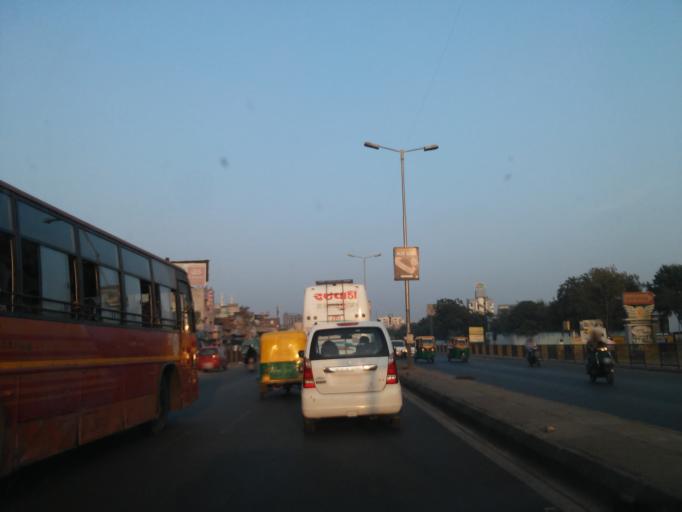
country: IN
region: Gujarat
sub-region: Ahmadabad
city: Sarkhej
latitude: 22.9937
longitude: 72.5260
